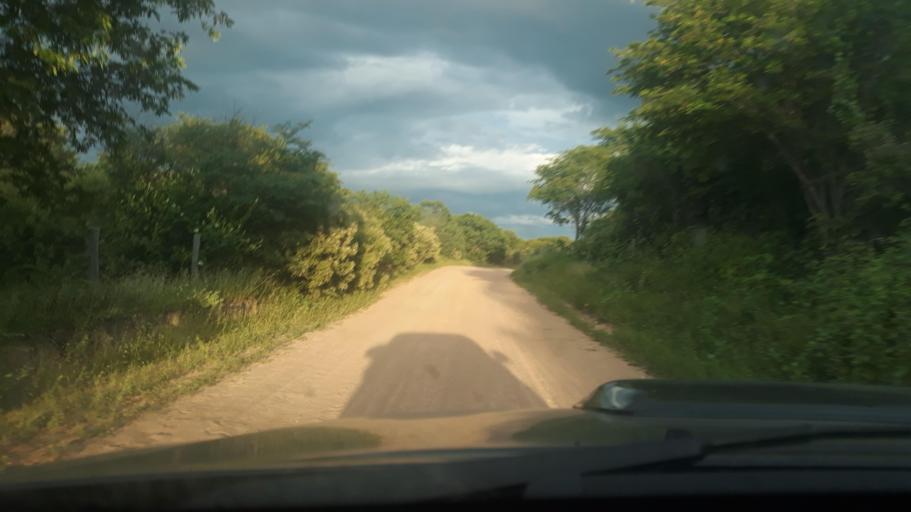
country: BR
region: Bahia
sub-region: Riacho De Santana
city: Riacho de Santana
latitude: -13.9091
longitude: -42.9447
